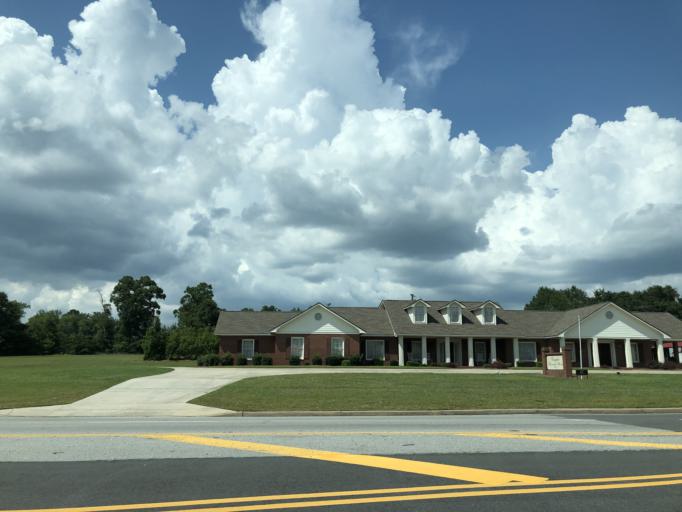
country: US
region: Georgia
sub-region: Telfair County
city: McRae
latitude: 32.0645
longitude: -82.8896
